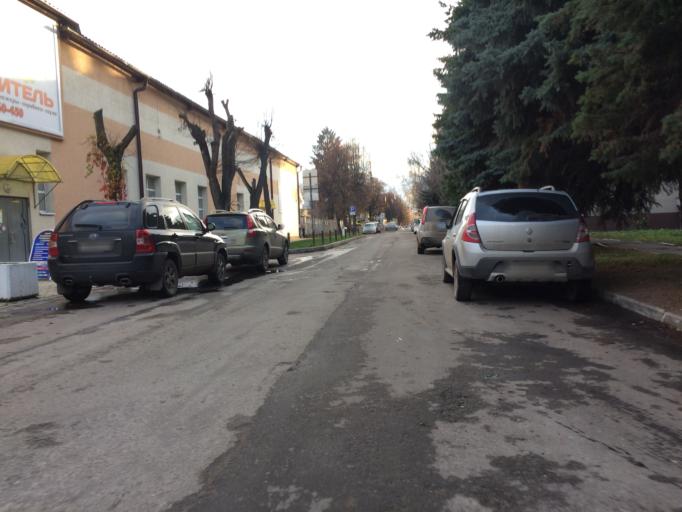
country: RU
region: Mariy-El
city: Yoshkar-Ola
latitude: 56.6414
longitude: 47.8994
